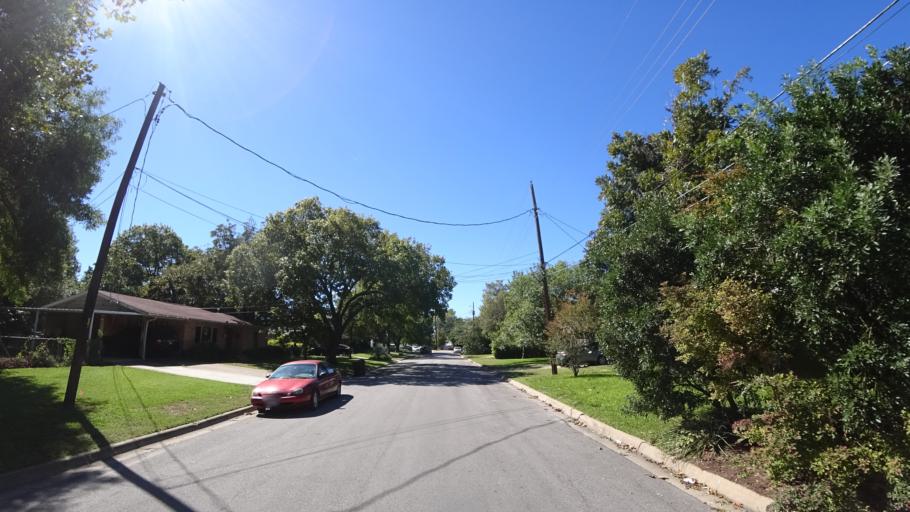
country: US
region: Texas
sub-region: Travis County
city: Austin
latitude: 30.3305
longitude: -97.7270
